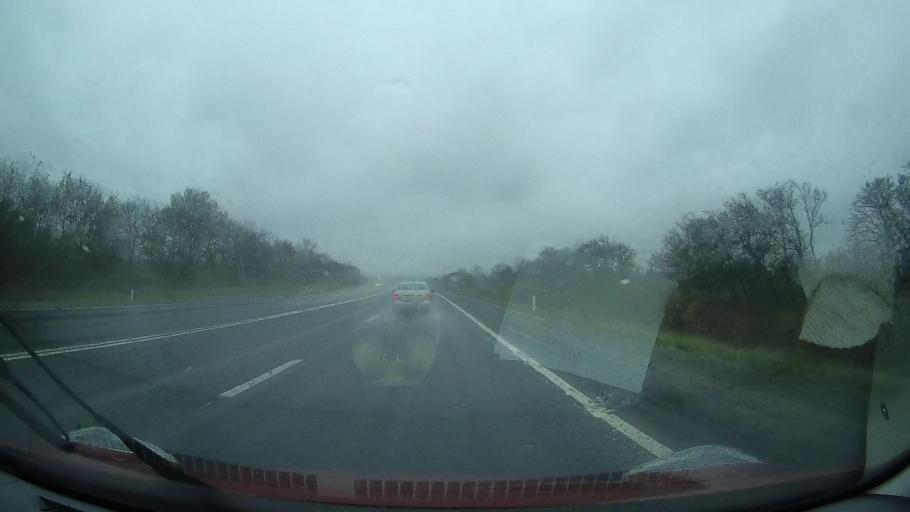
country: RU
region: Stavropol'skiy
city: Nevinnomyssk
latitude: 44.6195
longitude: 42.0939
